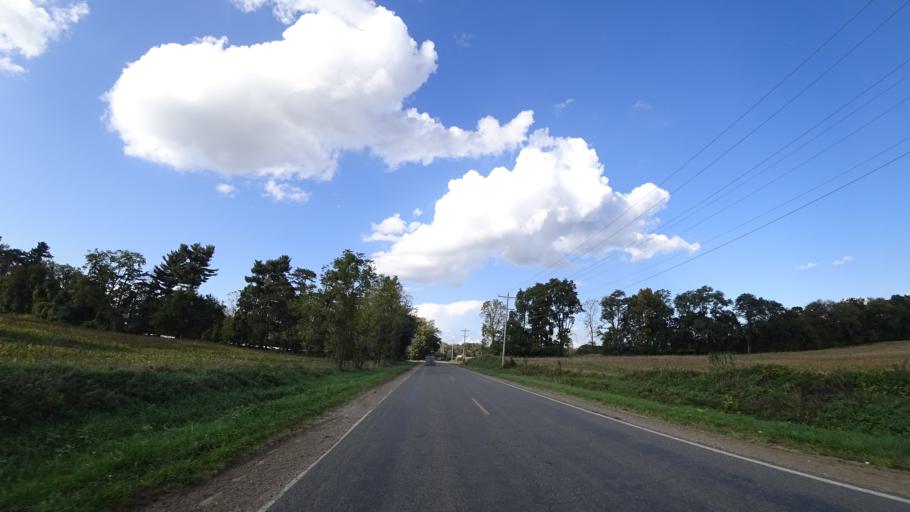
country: US
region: Michigan
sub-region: Saint Joseph County
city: Centreville
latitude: 41.9615
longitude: -85.5279
